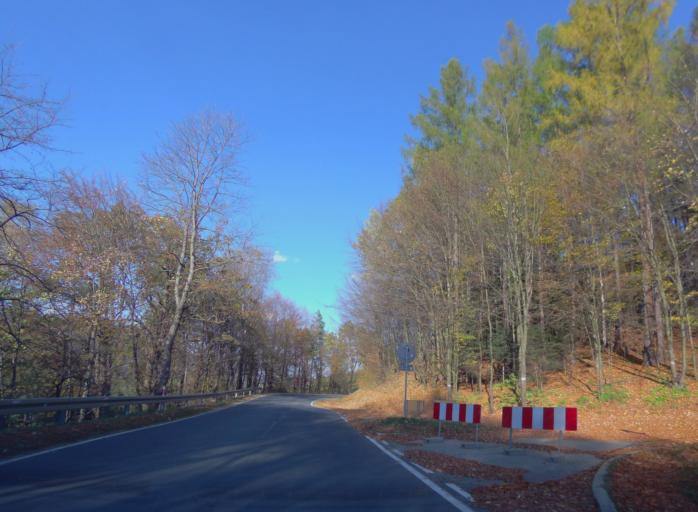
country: PL
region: Subcarpathian Voivodeship
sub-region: Powiat leski
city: Polanczyk
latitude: 49.3957
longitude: 22.4382
